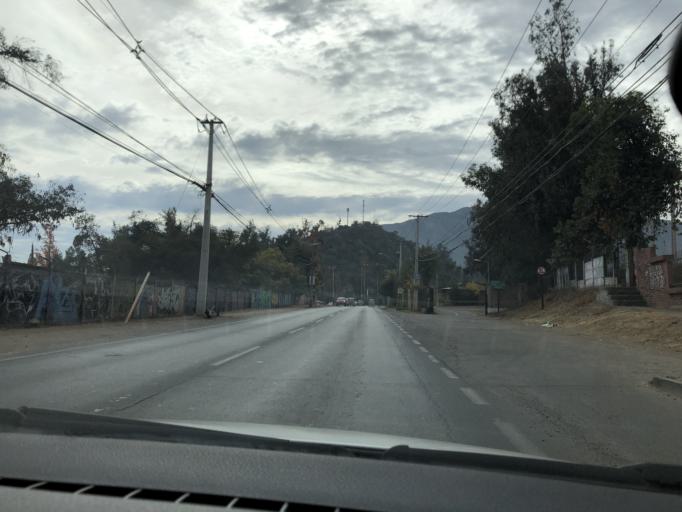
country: CL
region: Santiago Metropolitan
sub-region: Provincia de Cordillera
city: Puente Alto
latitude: -33.6005
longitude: -70.5317
